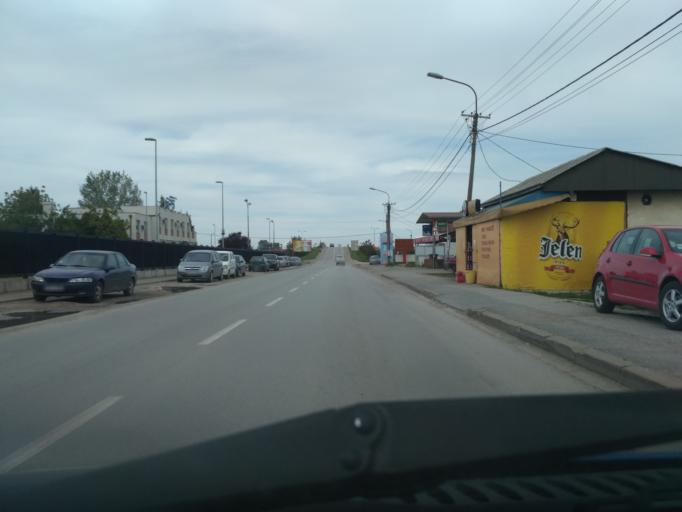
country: RS
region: Central Serbia
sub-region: Podunavski Okrug
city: Velika Plana
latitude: 44.3403
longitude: 21.0799
